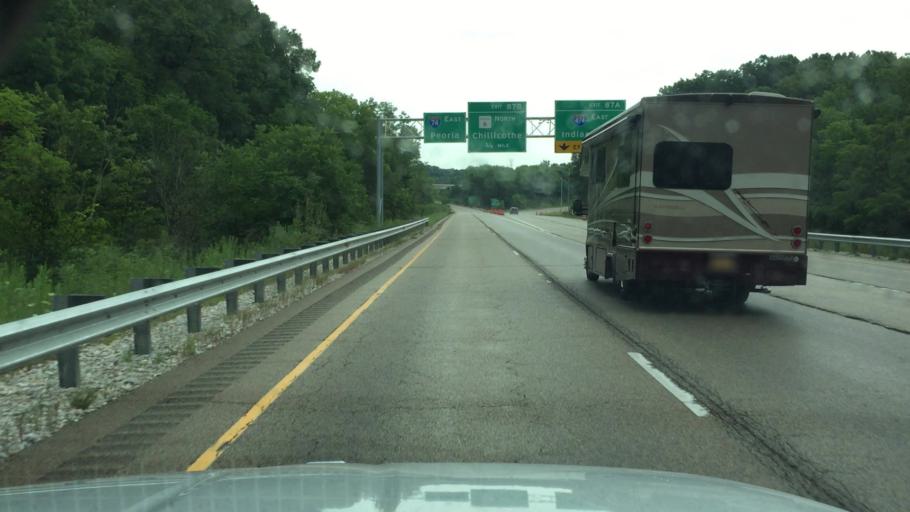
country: US
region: Illinois
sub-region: Peoria County
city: Bellevue
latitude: 40.7443
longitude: -89.6781
